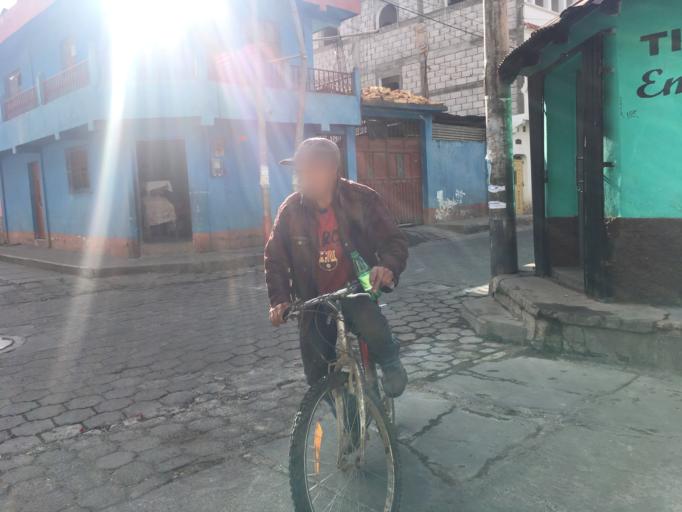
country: GT
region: Quetzaltenango
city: Ostuncalco
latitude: 14.8674
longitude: -91.6230
